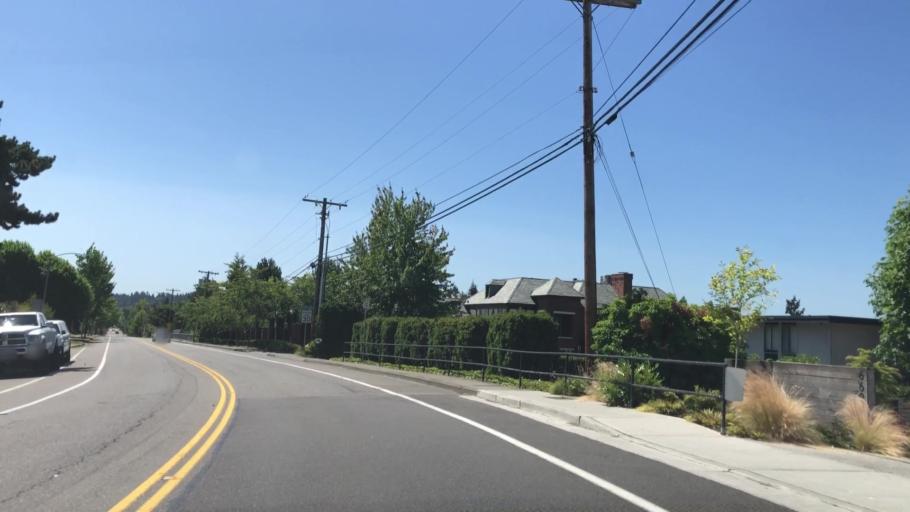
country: US
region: Washington
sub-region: King County
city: Kirkland
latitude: 47.6660
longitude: -122.2047
